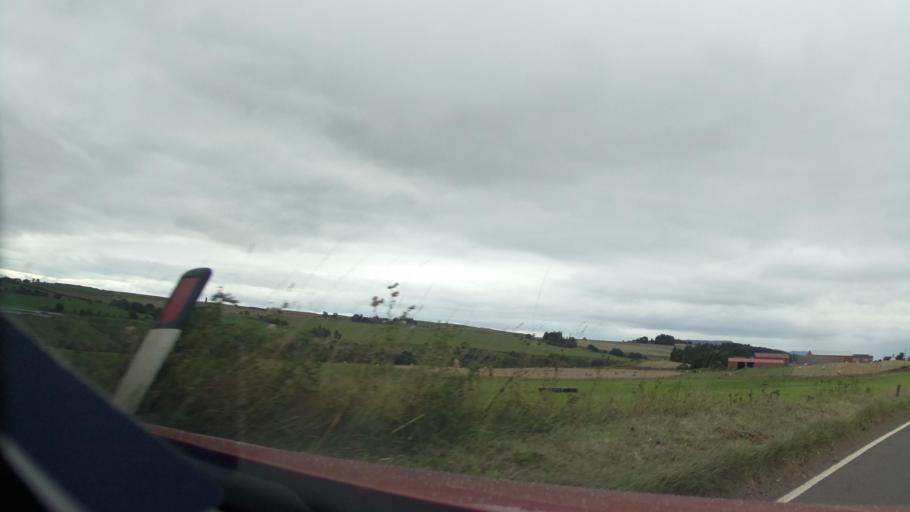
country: GB
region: Scotland
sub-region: Fife
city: Leslie
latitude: 56.2010
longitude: -3.2318
